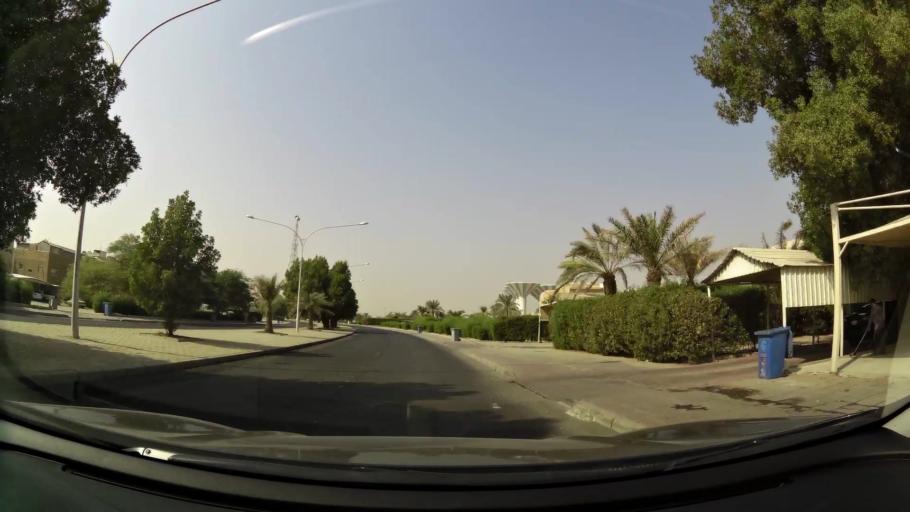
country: KW
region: Al Asimah
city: Ar Rabiyah
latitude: 29.2892
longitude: 47.8867
